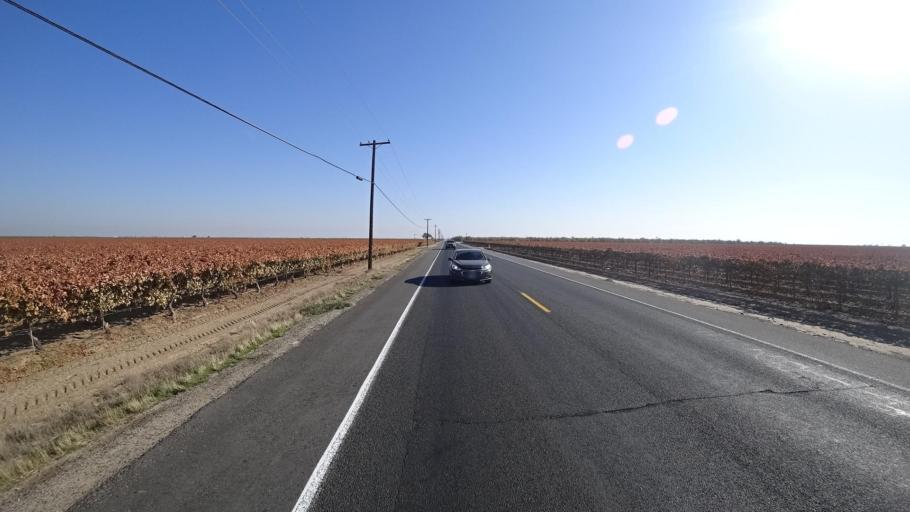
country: US
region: California
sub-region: Kern County
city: Delano
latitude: 35.7178
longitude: -119.2885
